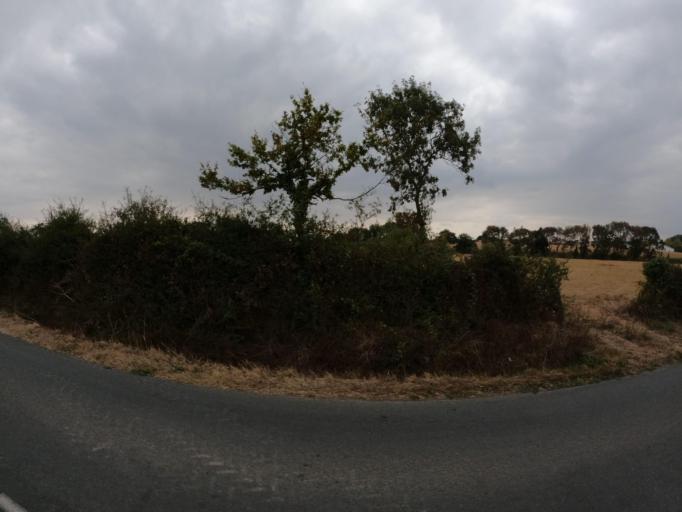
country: FR
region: Pays de la Loire
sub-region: Departement de la Vendee
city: La Guyonniere
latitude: 46.9711
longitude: -1.2455
